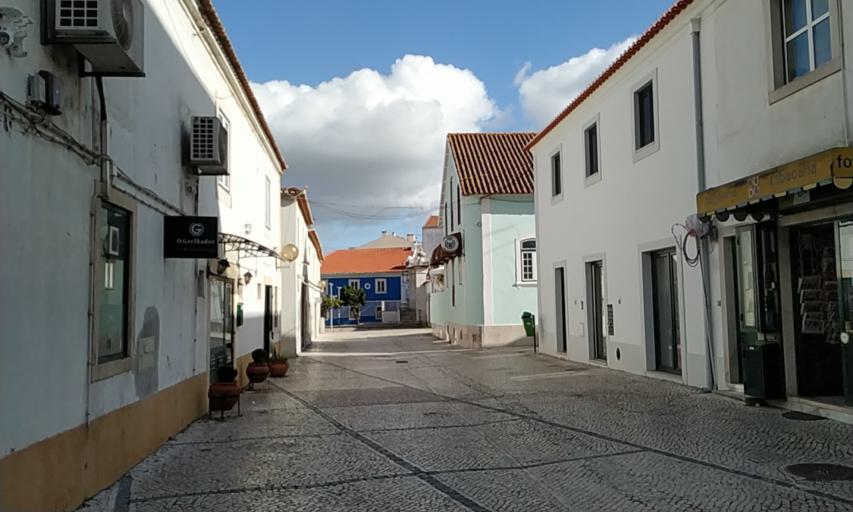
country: PT
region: Lisbon
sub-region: Loures
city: Loures
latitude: 38.8306
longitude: -9.1682
